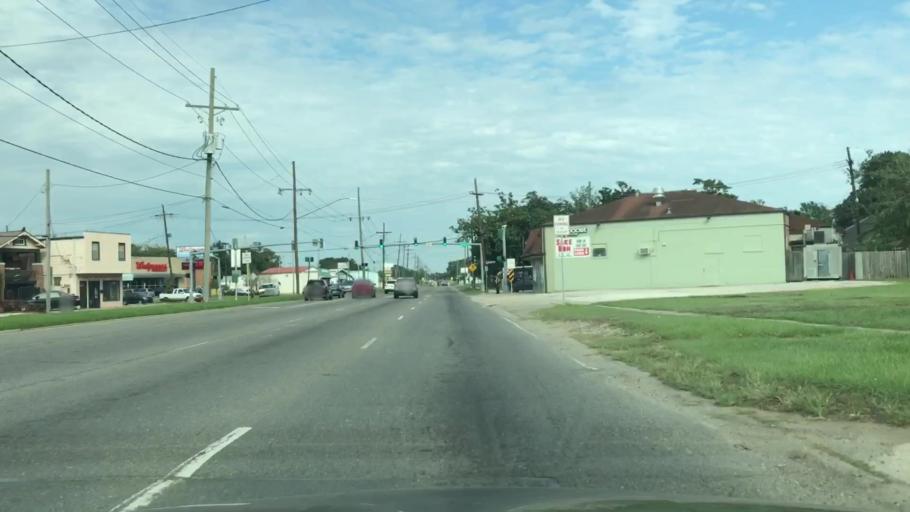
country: US
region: Louisiana
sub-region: Jefferson Parish
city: Elmwood
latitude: 29.9591
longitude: -90.1726
